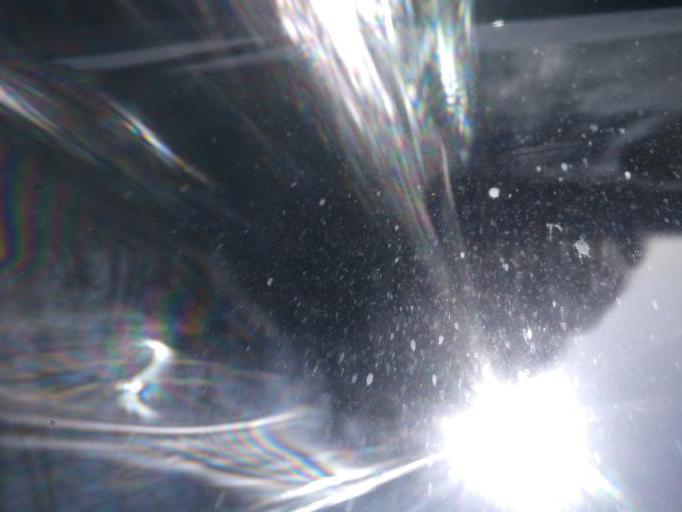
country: FR
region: Brittany
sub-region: Departement d'Ille-et-Vilaine
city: La Boussac
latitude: 48.5435
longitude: -1.6203
